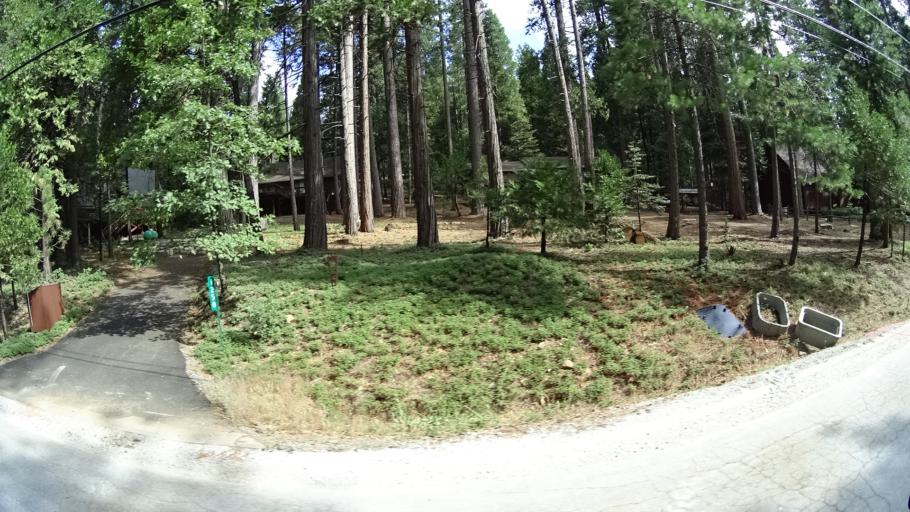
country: US
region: California
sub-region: Calaveras County
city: Arnold
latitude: 38.2533
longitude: -120.3379
